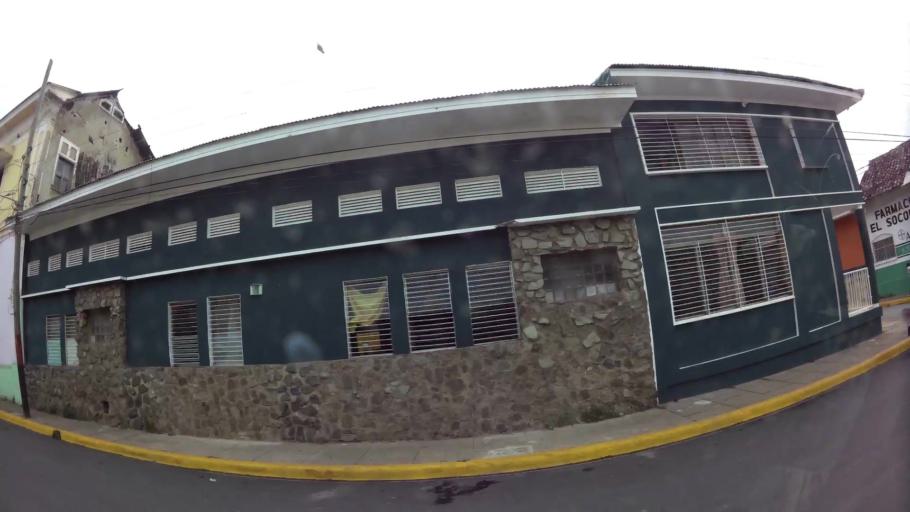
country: NI
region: Rivas
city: Rivas
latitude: 11.4379
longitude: -85.8325
